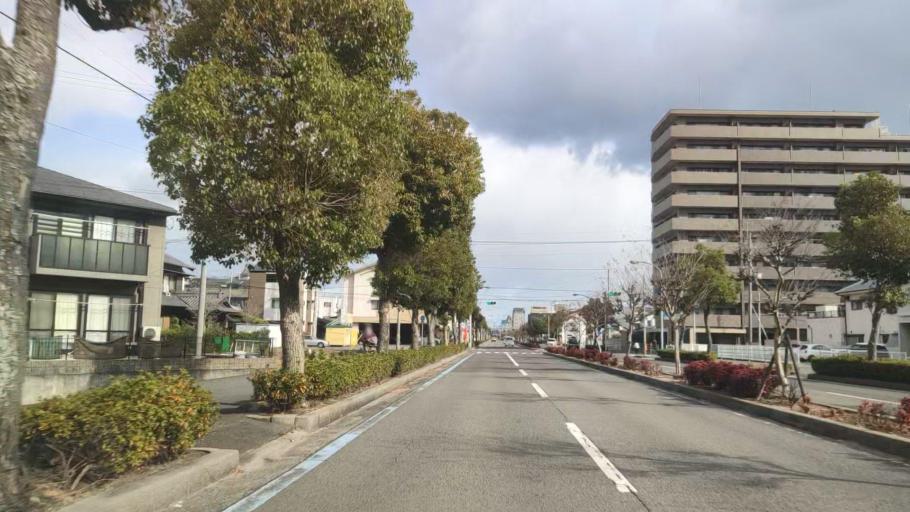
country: JP
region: Ehime
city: Hojo
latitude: 34.0607
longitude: 132.9843
